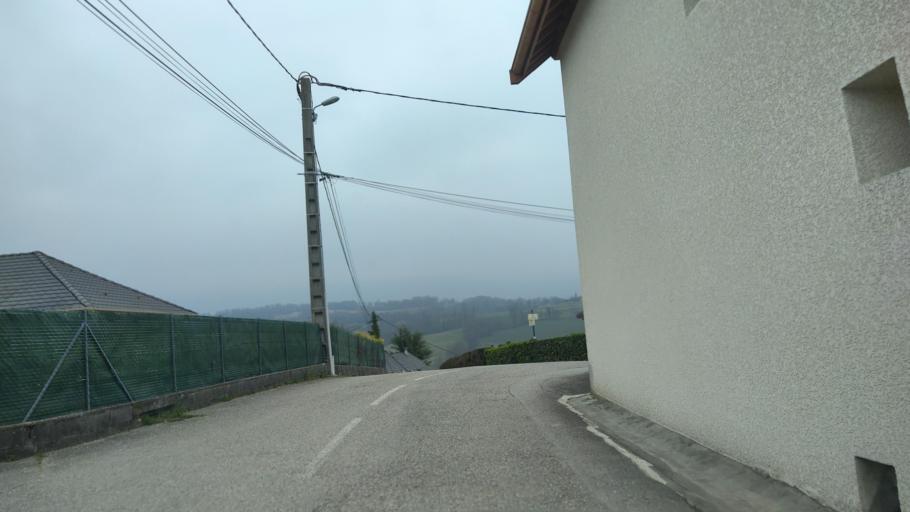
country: FR
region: Rhone-Alpes
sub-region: Departement de la Savoie
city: La Biolle
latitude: 45.7585
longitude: 5.9383
